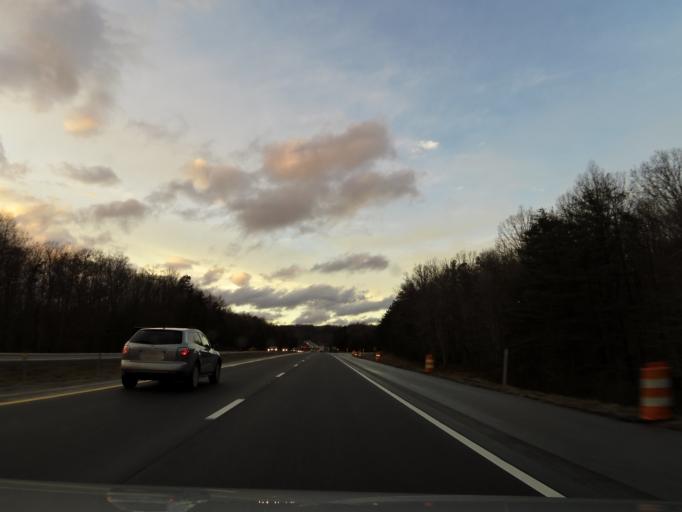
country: US
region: Tennessee
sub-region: Campbell County
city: Jacksboro
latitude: 36.4113
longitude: -84.2784
